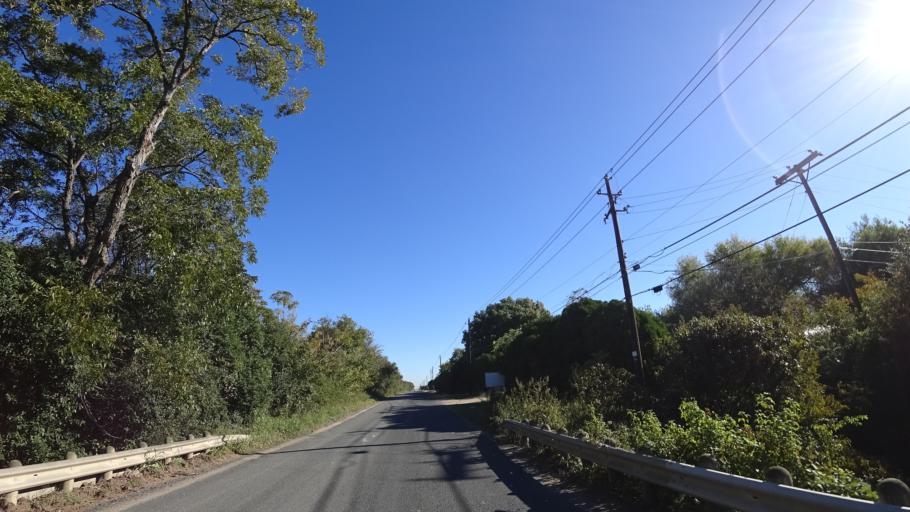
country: US
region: Texas
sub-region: Travis County
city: Austin
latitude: 30.2273
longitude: -97.6740
